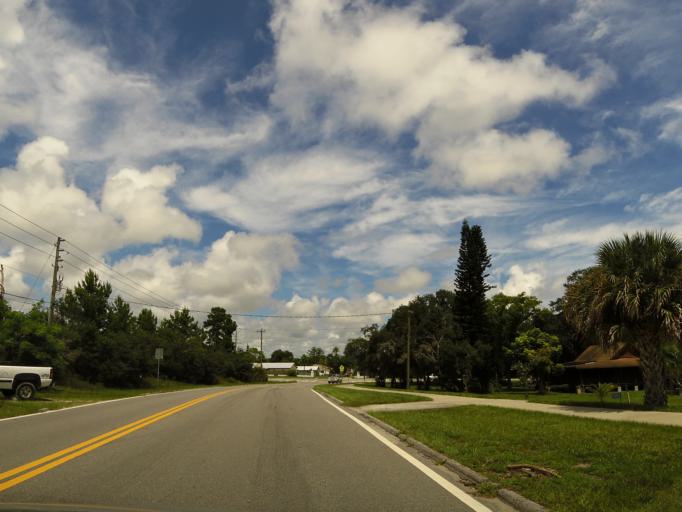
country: US
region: Florida
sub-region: Brevard County
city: Mims
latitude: 28.6360
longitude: -80.8542
